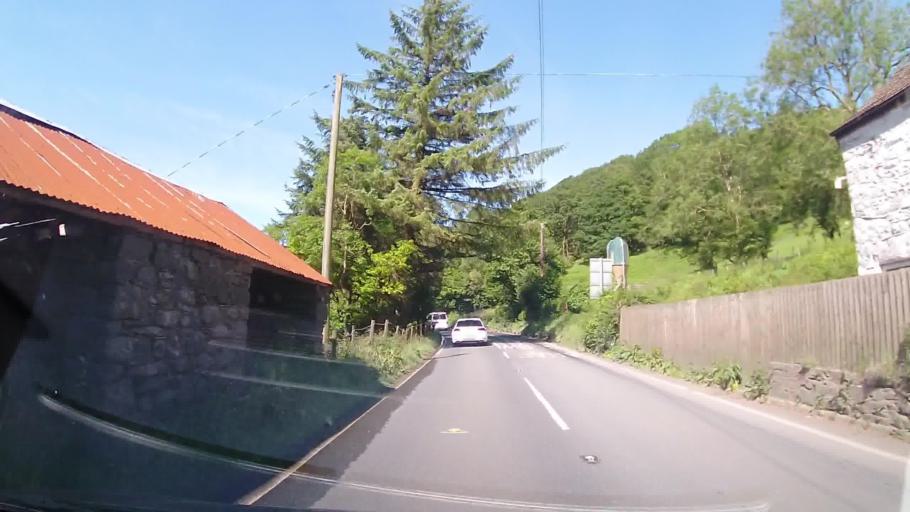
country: GB
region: Wales
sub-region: Gwynedd
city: Bala
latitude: 52.6985
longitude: -3.6250
